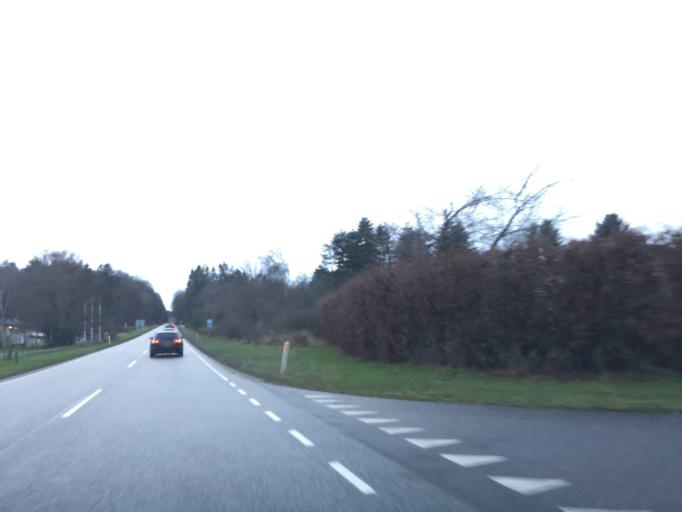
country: DK
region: Central Jutland
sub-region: Viborg Kommune
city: Bjerringbro
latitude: 56.3122
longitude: 9.5836
